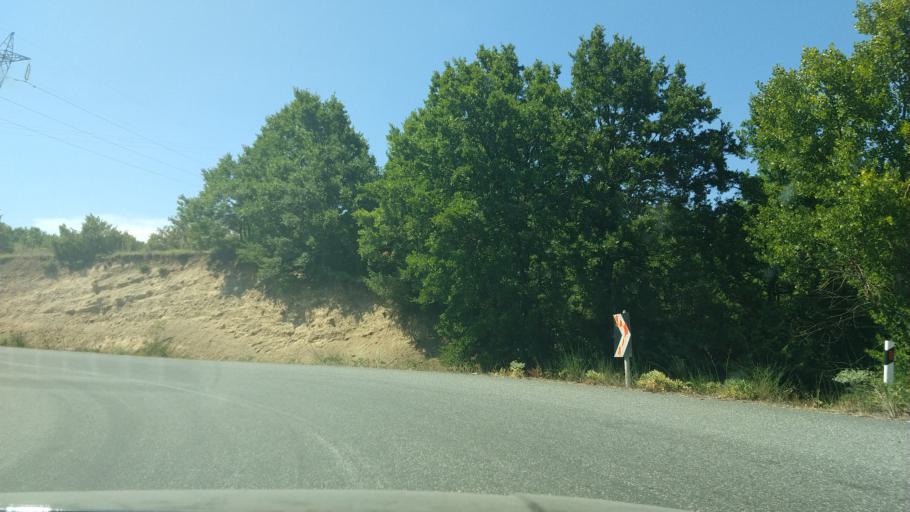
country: GR
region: West Macedonia
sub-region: Nomos Grevenon
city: Grevena
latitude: 40.0507
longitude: 21.4735
